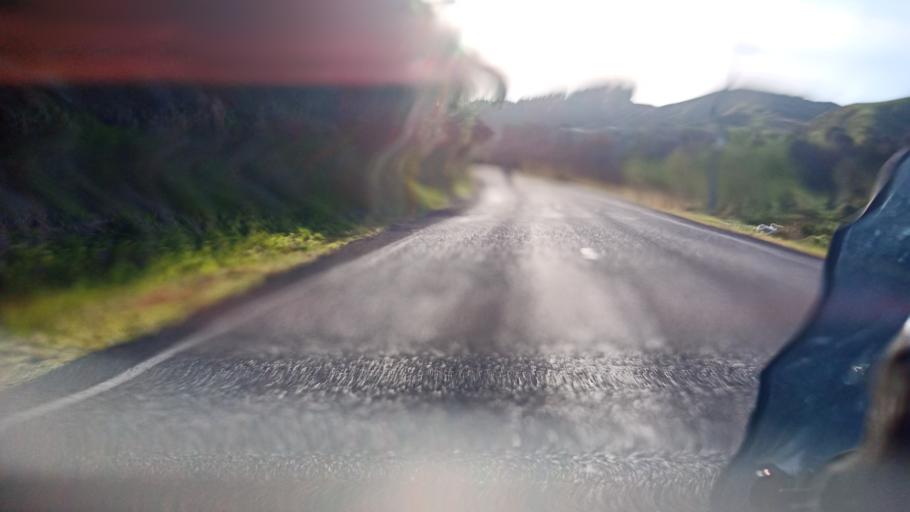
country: NZ
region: Gisborne
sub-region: Gisborne District
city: Gisborne
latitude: -38.4589
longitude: 177.6439
